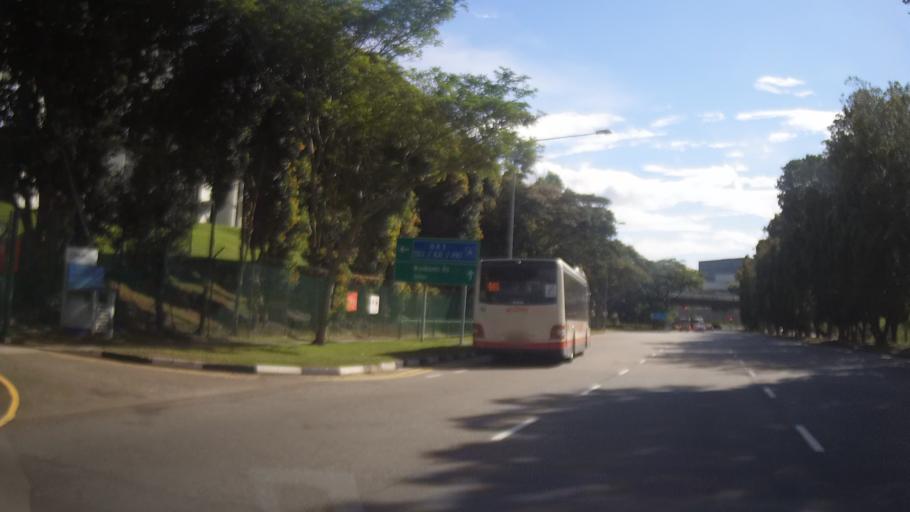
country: MY
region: Johor
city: Johor Bahru
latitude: 1.4318
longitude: 103.7711
